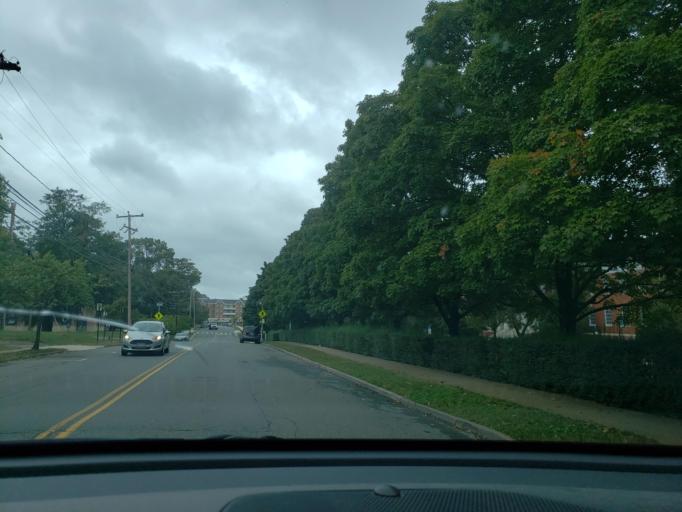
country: US
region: Virginia
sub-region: City of Fredericksburg
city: Fredericksburg
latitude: 38.3041
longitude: -77.4778
